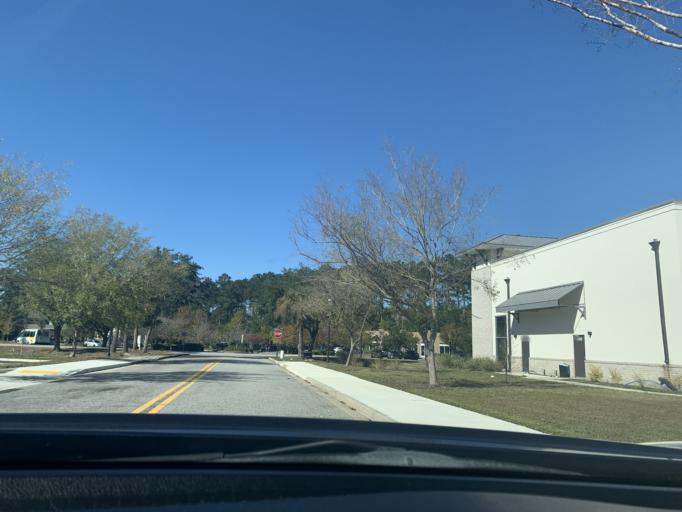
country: US
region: Georgia
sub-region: Chatham County
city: Pooler
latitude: 32.1345
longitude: -81.2575
